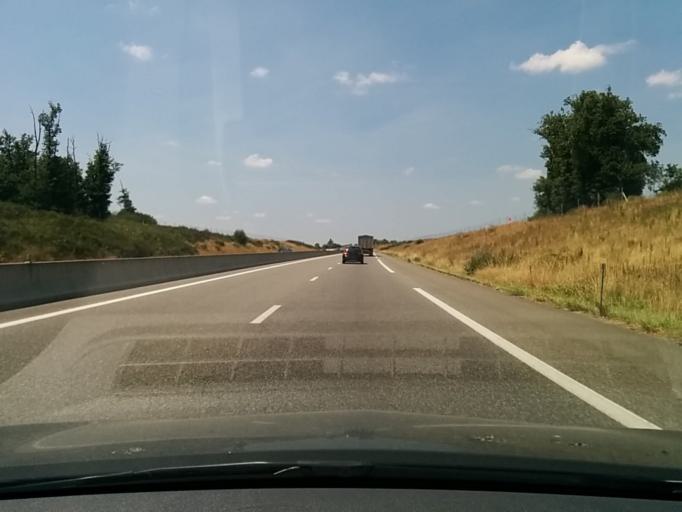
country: FR
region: Midi-Pyrenees
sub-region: Departement de la Haute-Garonne
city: La Salvetat-Saint-Gilles
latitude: 43.5853
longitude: 1.2617
